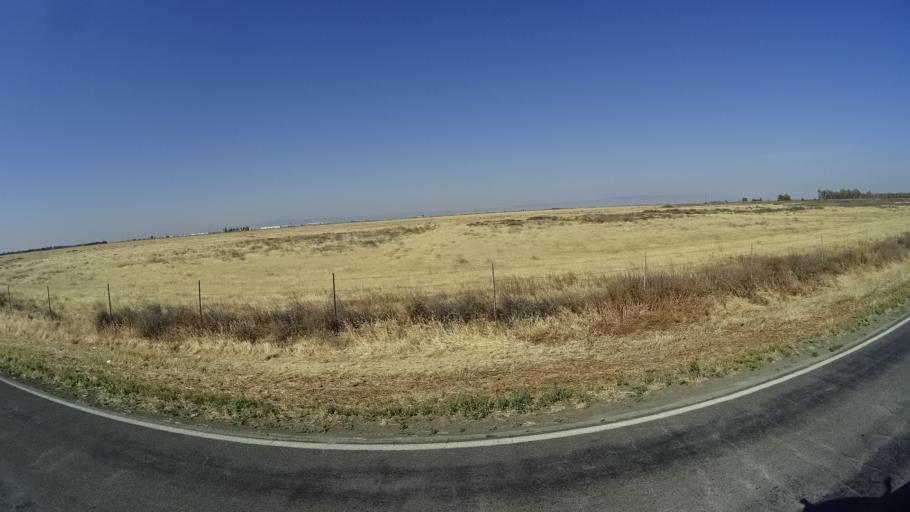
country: US
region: California
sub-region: Fresno County
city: Riverdale
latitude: 36.3692
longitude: -119.9203
